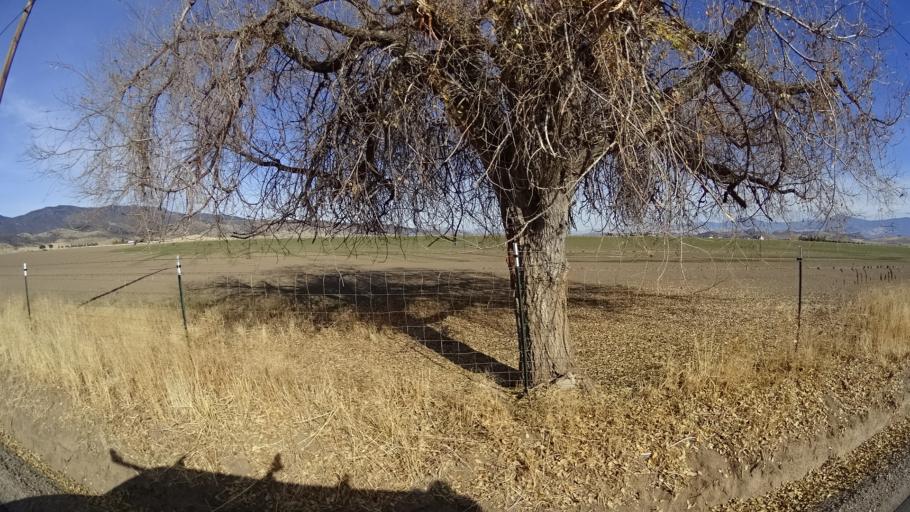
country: US
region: California
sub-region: Siskiyou County
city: Montague
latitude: 41.5381
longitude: -122.5457
